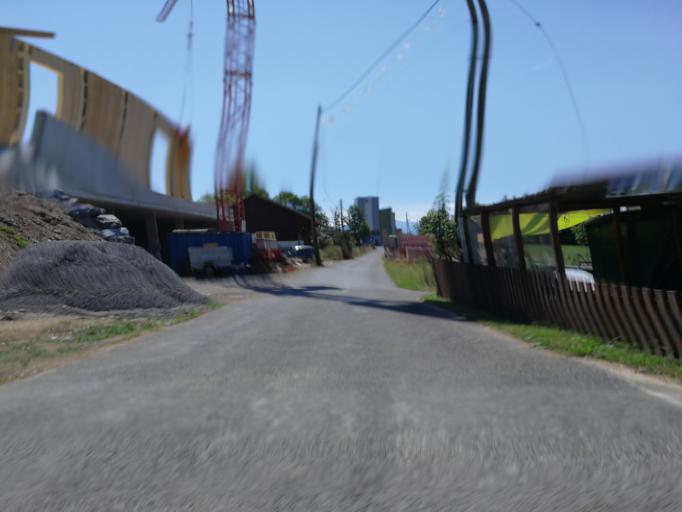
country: CH
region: Zurich
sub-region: Bezirk Hinwil
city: Gossau
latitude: 47.3154
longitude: 8.7506
